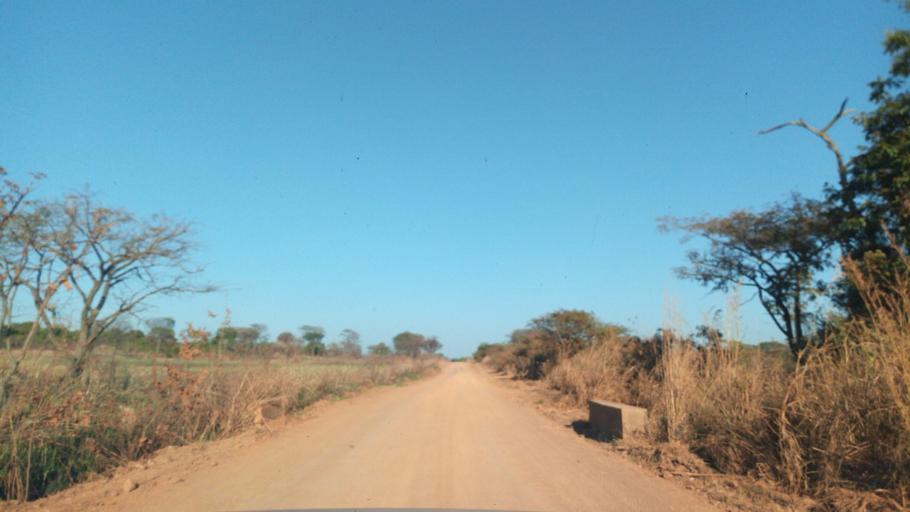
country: ZM
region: Luapula
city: Mwense
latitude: -10.4524
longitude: 28.5520
